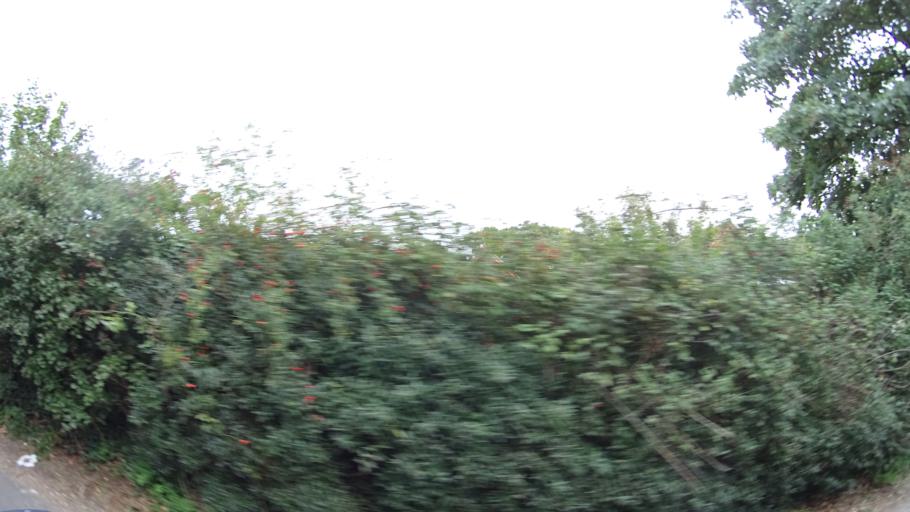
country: GB
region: England
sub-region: Hampshire
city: Romsey
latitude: 51.0043
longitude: -1.5214
